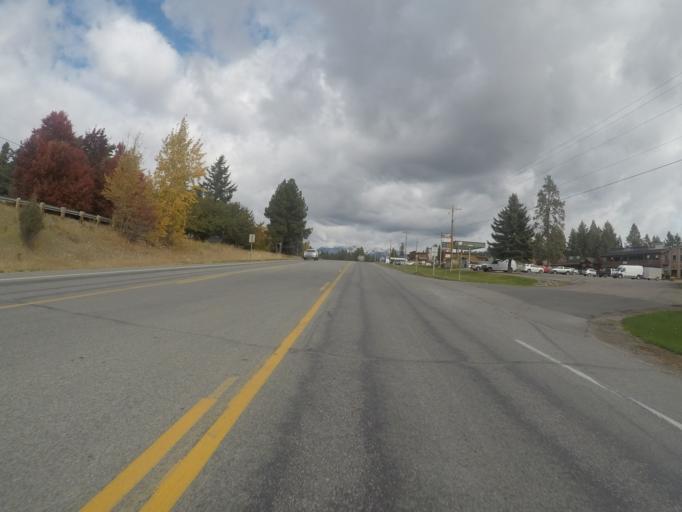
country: US
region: Montana
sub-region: Flathead County
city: Bigfork
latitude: 48.0718
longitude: -114.0797
